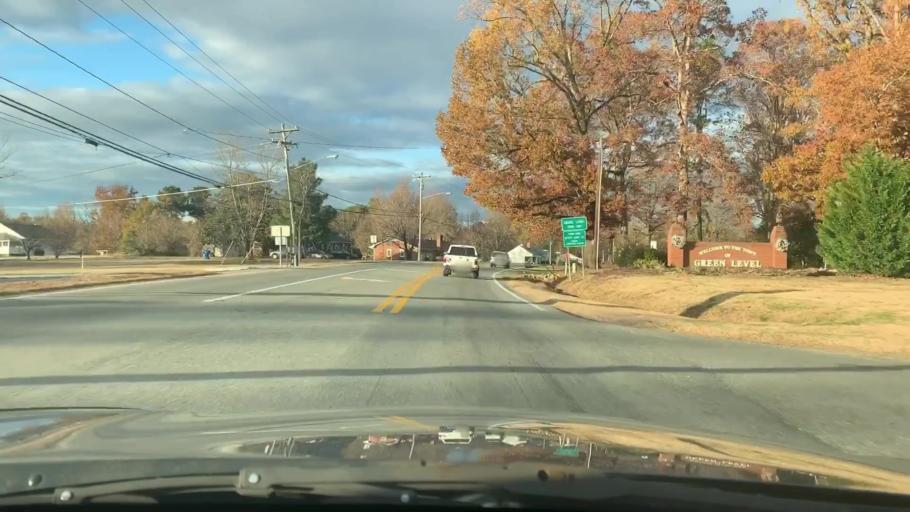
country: US
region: North Carolina
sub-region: Alamance County
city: Green Level
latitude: 36.1133
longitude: -79.3538
